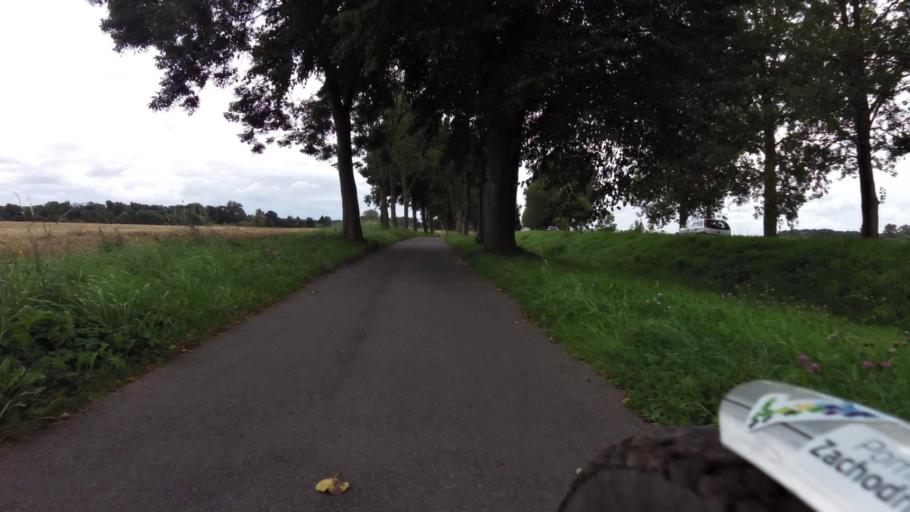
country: PL
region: West Pomeranian Voivodeship
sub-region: Powiat koszalinski
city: Mielno
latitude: 54.2285
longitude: 16.0758
